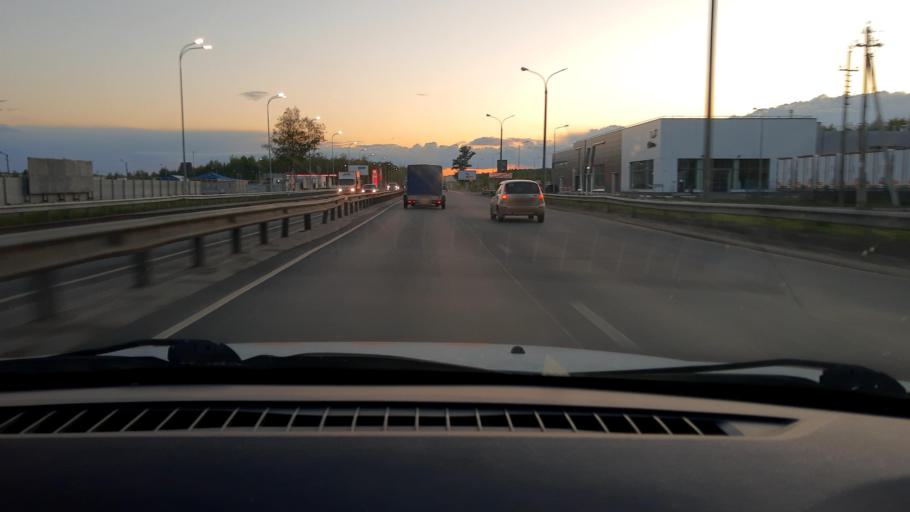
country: RU
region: Nizjnij Novgorod
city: Gorbatovka
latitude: 56.3102
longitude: 43.7928
